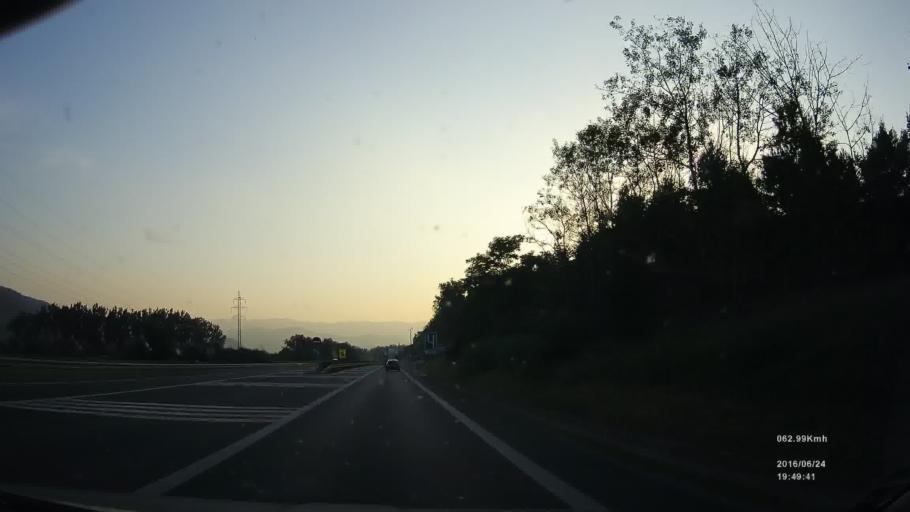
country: SK
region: Banskobystricky
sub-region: Okres Banska Bystrica
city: Banska Bystrica
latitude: 48.7422
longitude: 19.2052
